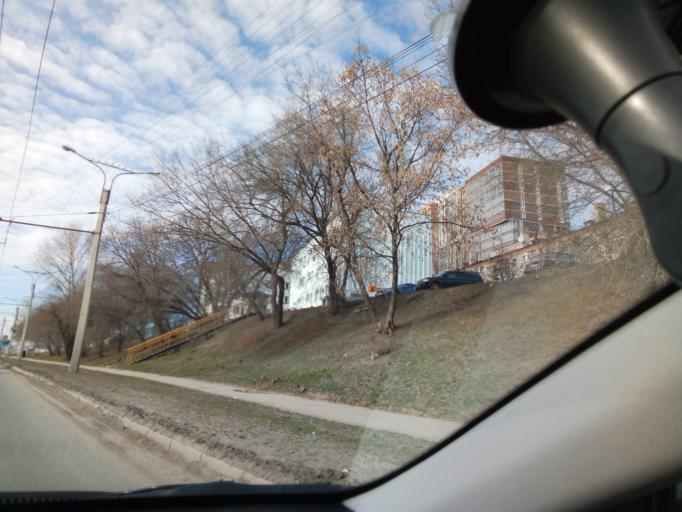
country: RU
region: Chuvashia
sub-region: Cheboksarskiy Rayon
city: Cheboksary
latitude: 56.1189
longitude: 47.2525
